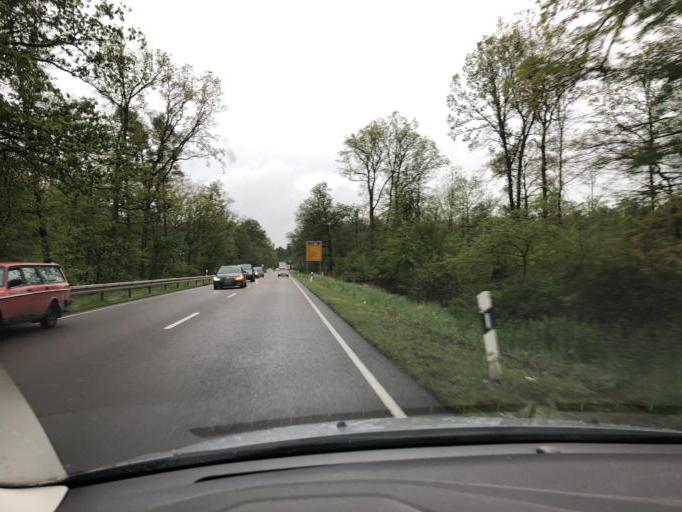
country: DE
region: Saxony-Anhalt
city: Raguhn
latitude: 51.7618
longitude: 12.2267
